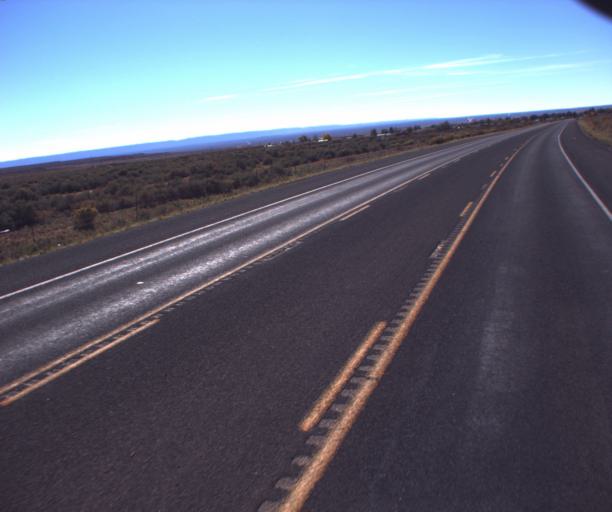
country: US
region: Arizona
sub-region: Coconino County
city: Fredonia
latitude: 36.9678
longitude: -112.5271
